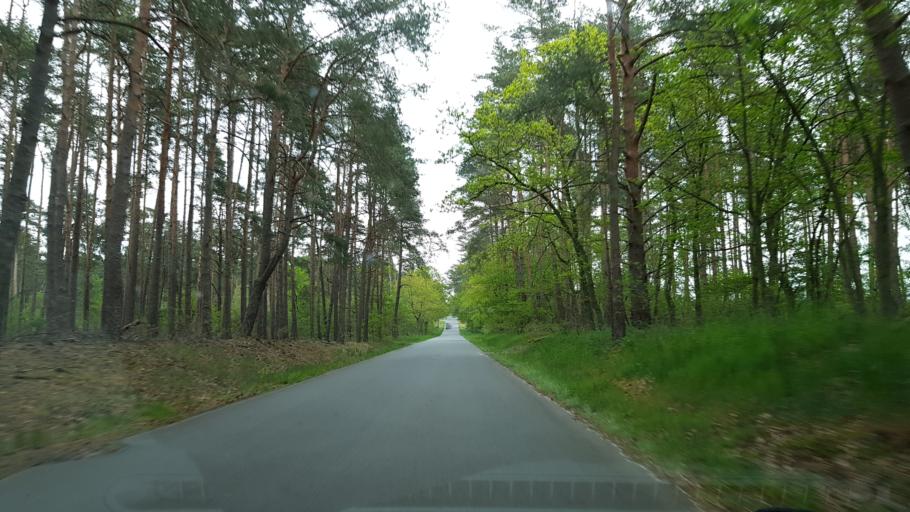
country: DE
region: Lower Saxony
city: Gartow
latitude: 53.0568
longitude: 11.4455
